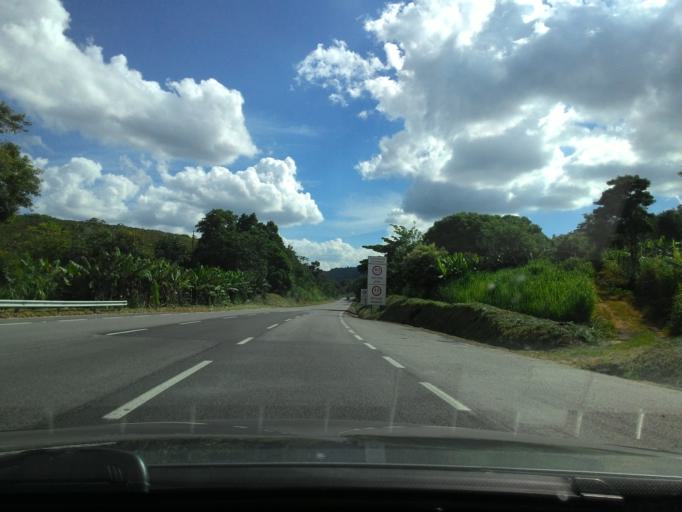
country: BR
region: Sao Paulo
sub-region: Cajati
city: Cajati
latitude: -24.7807
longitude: -48.1748
